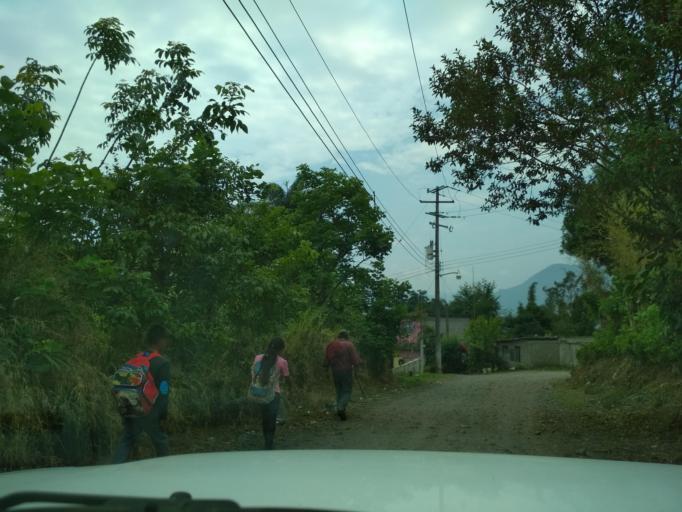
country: MX
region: Veracruz
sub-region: Mariano Escobedo
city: Mariano Escobedo
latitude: 18.9207
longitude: -97.1271
